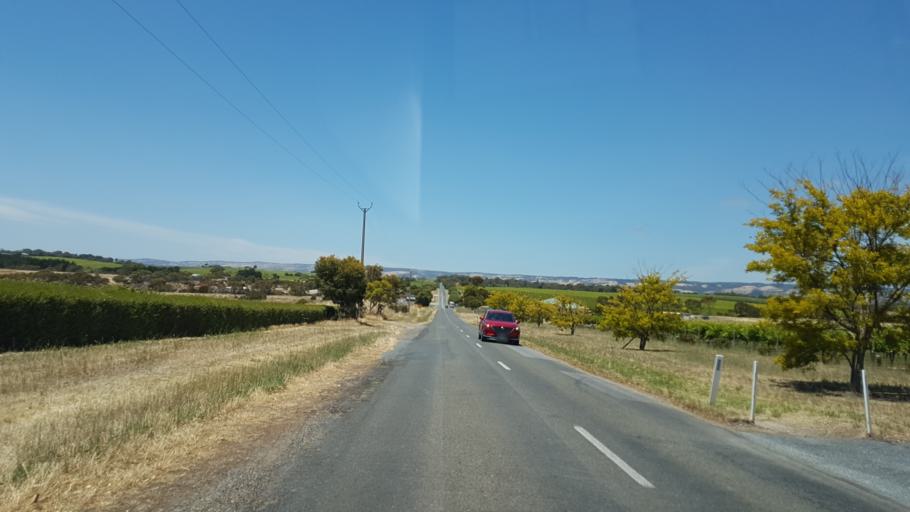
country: AU
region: South Australia
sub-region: Onkaparinga
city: Moana
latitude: -35.2327
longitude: 138.4894
